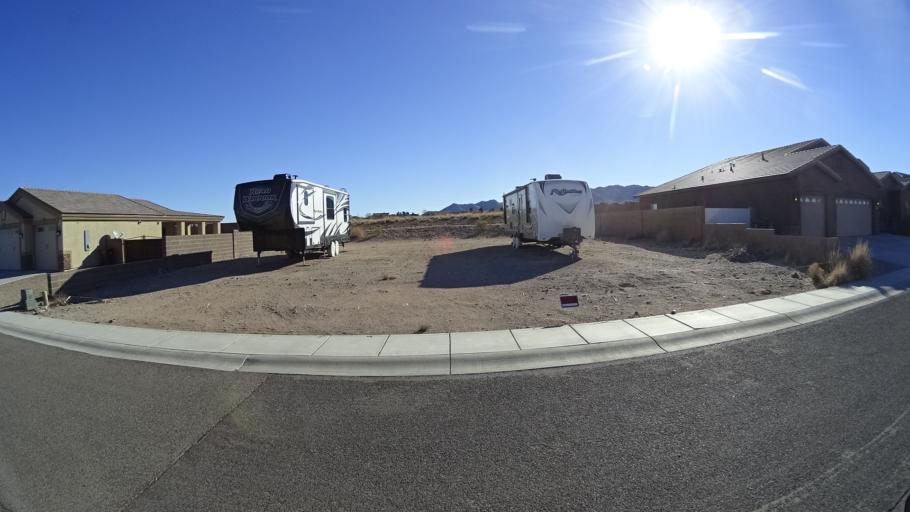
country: US
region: Arizona
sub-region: Mohave County
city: Kingman
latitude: 35.1867
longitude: -113.9988
